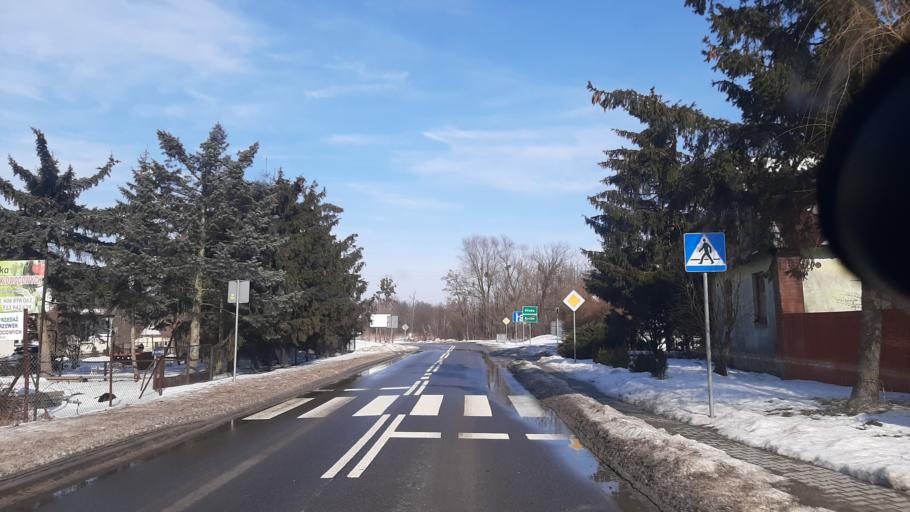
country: PL
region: Lublin Voivodeship
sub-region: Powiat pulawski
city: Kurow
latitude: 51.4094
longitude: 22.2060
